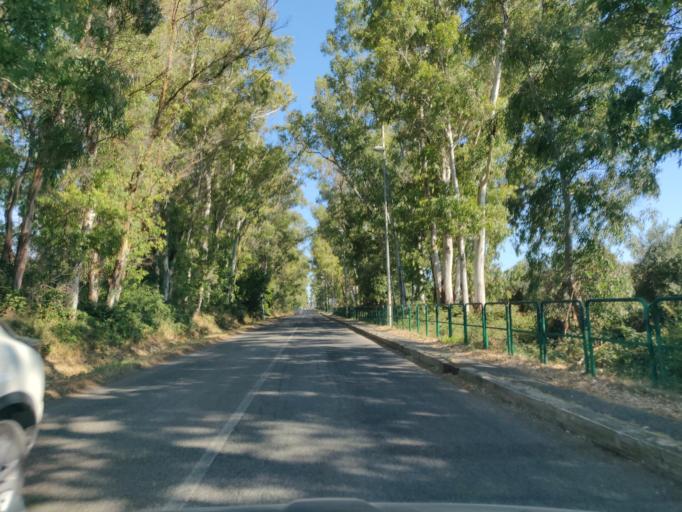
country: IT
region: Latium
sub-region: Citta metropolitana di Roma Capitale
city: Aurelia
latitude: 42.1441
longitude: 11.7636
